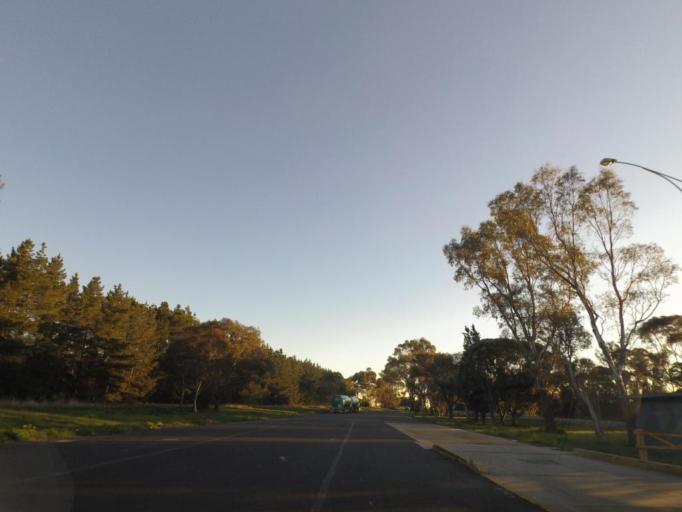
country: AU
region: Victoria
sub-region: Hume
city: Craigieburn
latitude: -37.4972
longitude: 144.9590
